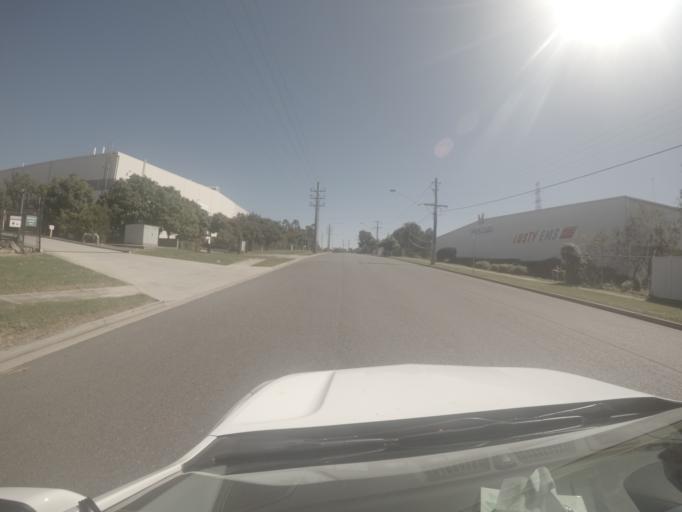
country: AU
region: Queensland
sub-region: Brisbane
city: Richlands
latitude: -27.5804
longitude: 152.9502
